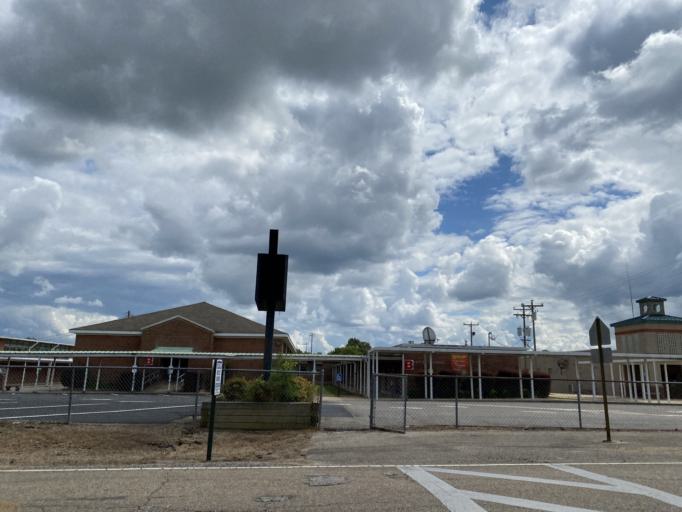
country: US
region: Mississippi
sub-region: Monroe County
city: Amory
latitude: 33.9770
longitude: -88.4160
